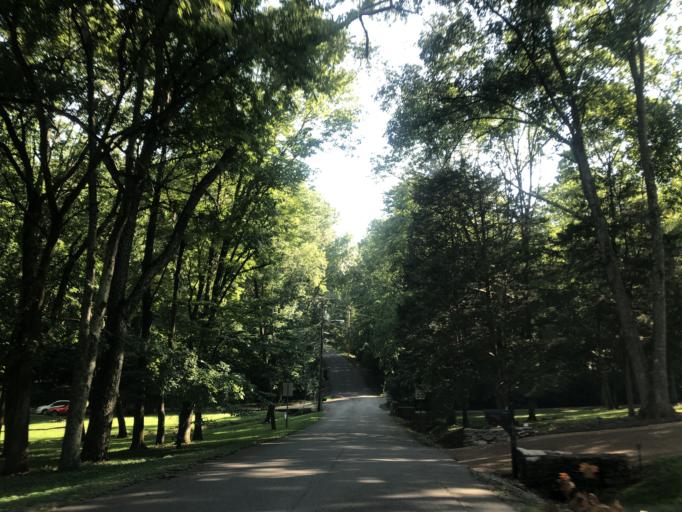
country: US
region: Tennessee
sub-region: Davidson County
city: Nashville
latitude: 36.2356
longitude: -86.8367
